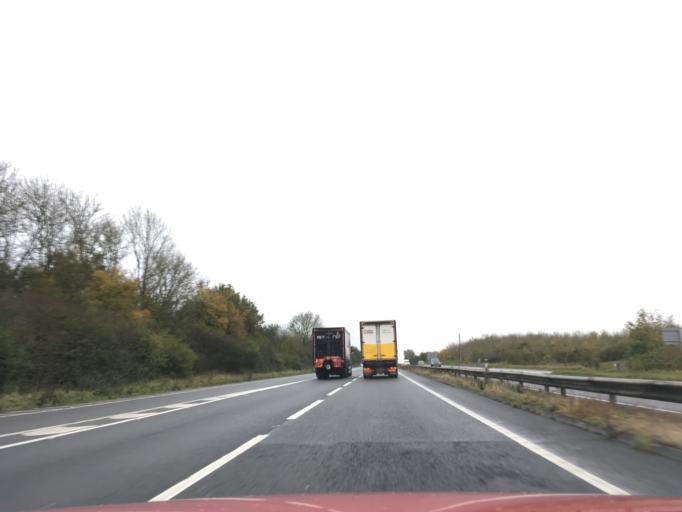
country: GB
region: England
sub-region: Hampshire
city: Overton
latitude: 51.2154
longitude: -1.3416
